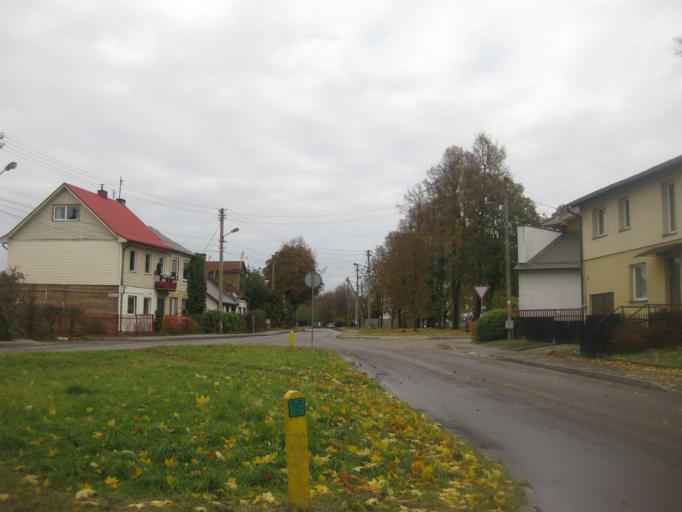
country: LT
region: Kauno apskritis
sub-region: Kaunas
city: Kaunas
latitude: 54.9119
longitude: 23.9180
